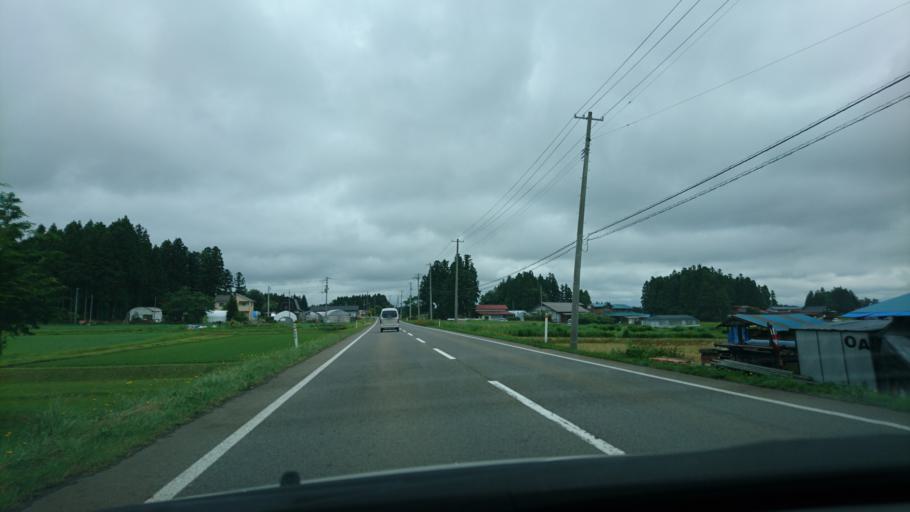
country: JP
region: Iwate
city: Mizusawa
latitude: 39.1086
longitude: 141.0525
